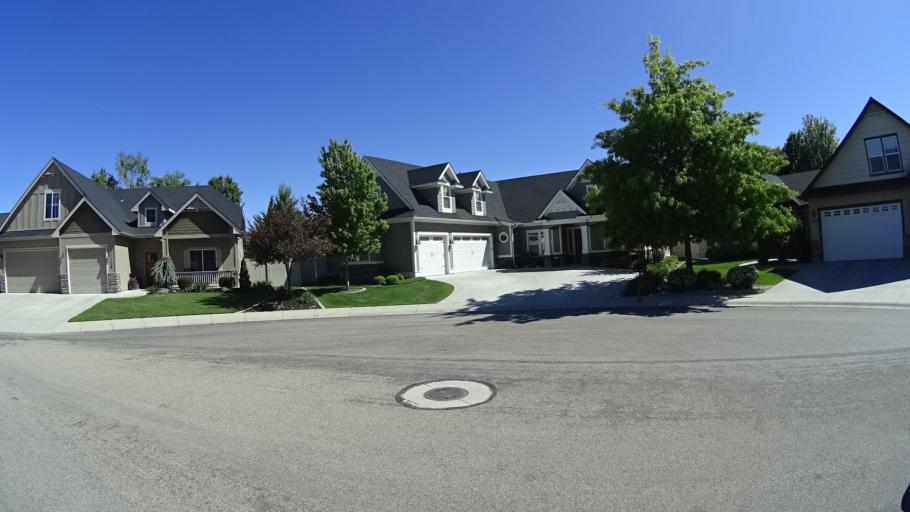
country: US
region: Idaho
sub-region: Ada County
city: Meridian
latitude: 43.6424
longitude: -116.3851
